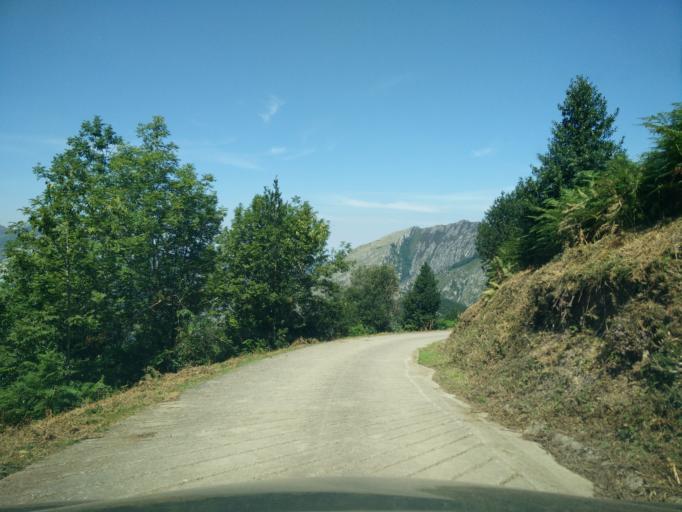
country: ES
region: Asturias
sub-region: Province of Asturias
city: Amieva
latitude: 43.1874
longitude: -5.1429
